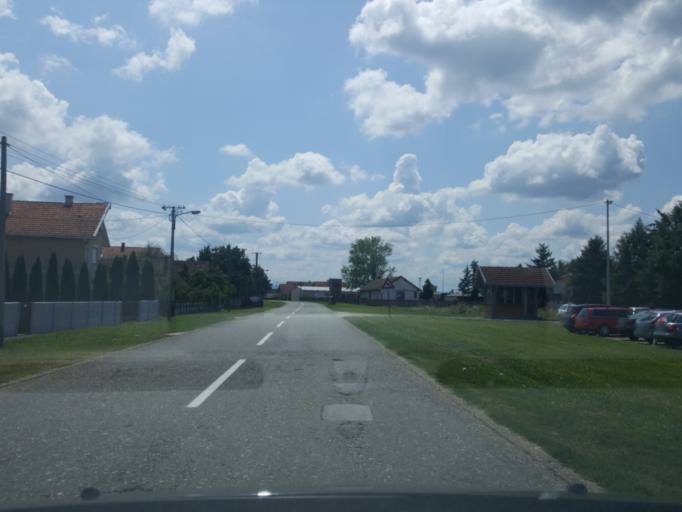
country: RS
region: Central Serbia
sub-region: Macvanski Okrug
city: Bogatic
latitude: 44.8225
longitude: 19.4775
